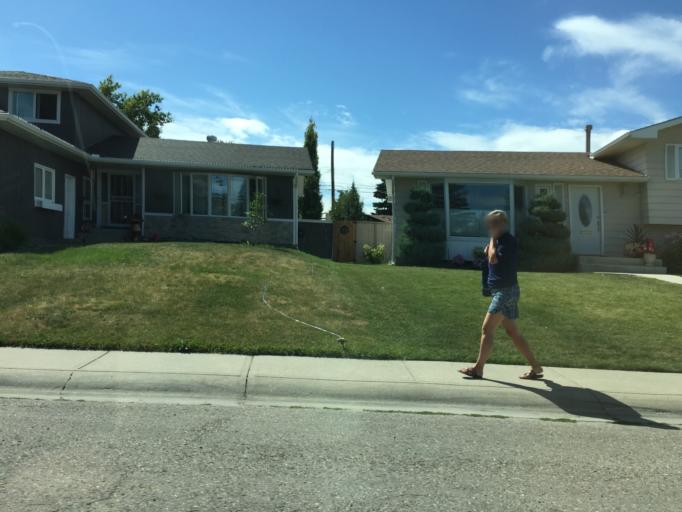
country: CA
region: Alberta
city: Calgary
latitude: 50.9326
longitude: -114.0389
